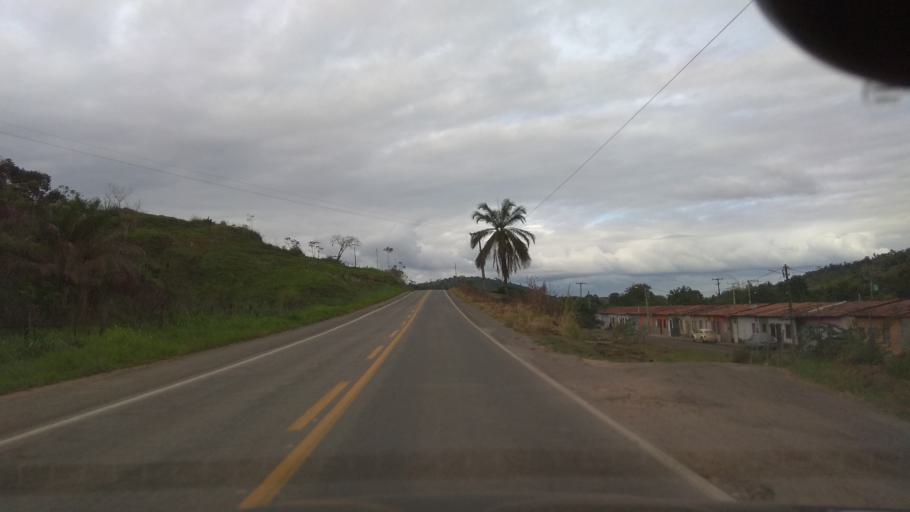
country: BR
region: Bahia
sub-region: Ipiau
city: Ipiau
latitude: -14.1439
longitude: -39.7164
